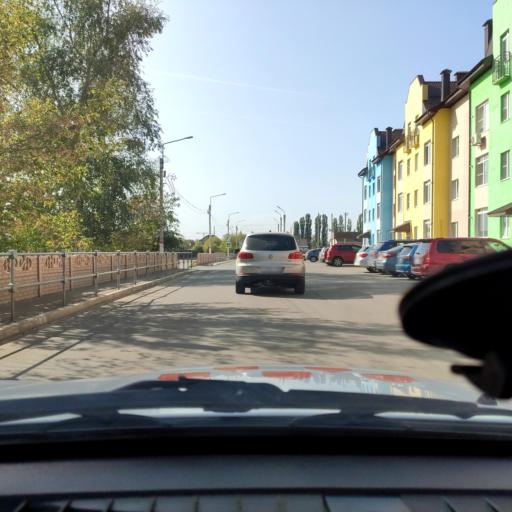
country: RU
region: Voronezj
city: Novaya Usman'
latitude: 51.6537
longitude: 39.3336
